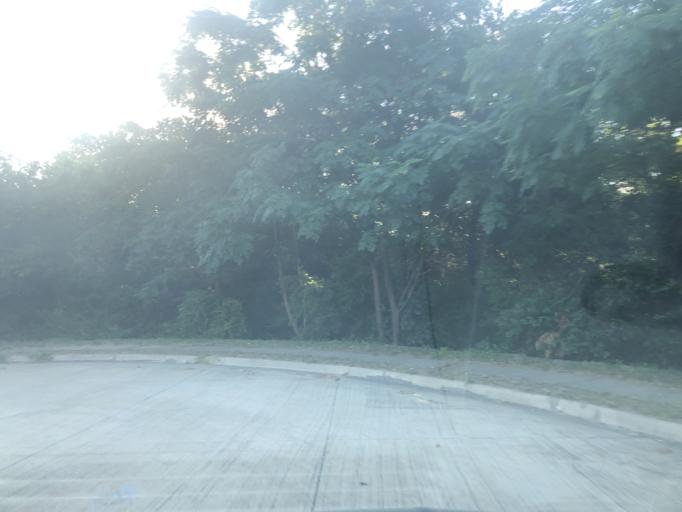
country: US
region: Texas
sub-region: Dallas County
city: Duncanville
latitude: 32.6619
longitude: -96.9507
